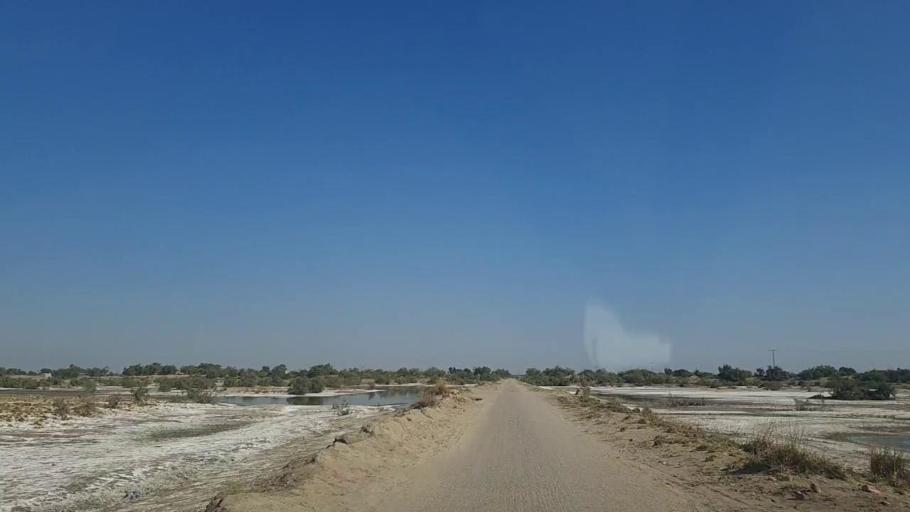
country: PK
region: Sindh
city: Sanghar
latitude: 26.2206
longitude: 68.9534
